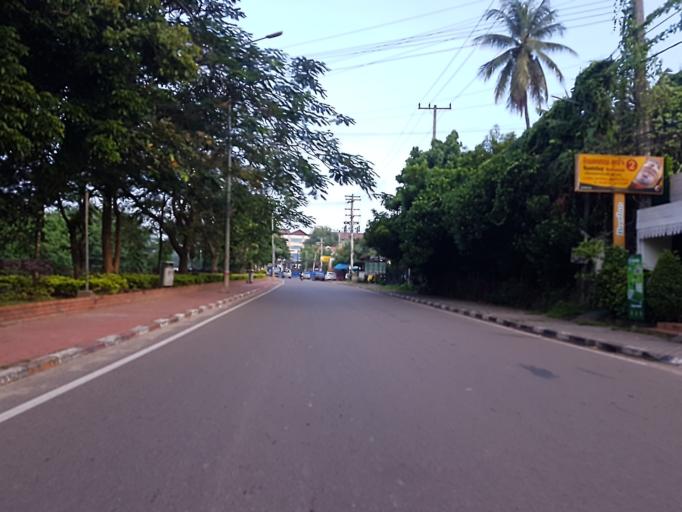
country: LA
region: Vientiane
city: Vientiane
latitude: 17.9546
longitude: 102.6166
